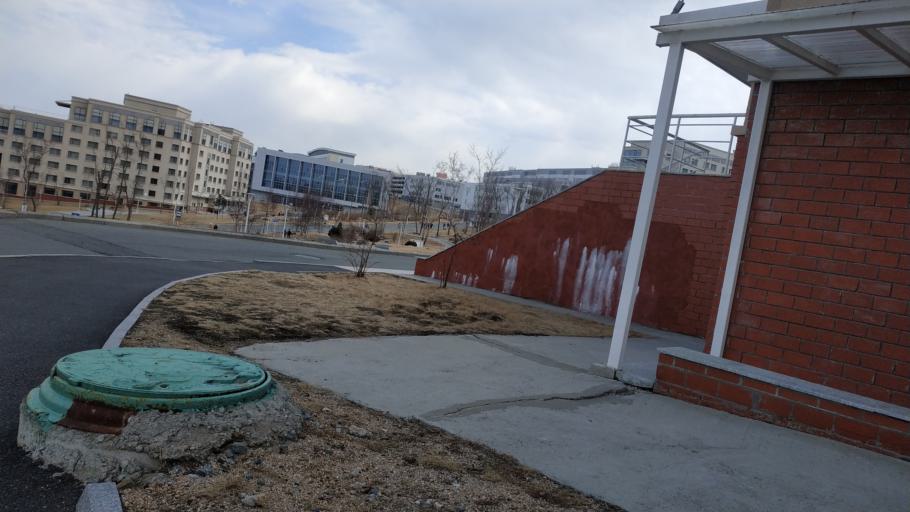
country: RU
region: Primorskiy
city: Russkiy
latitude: 43.0289
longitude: 131.8868
